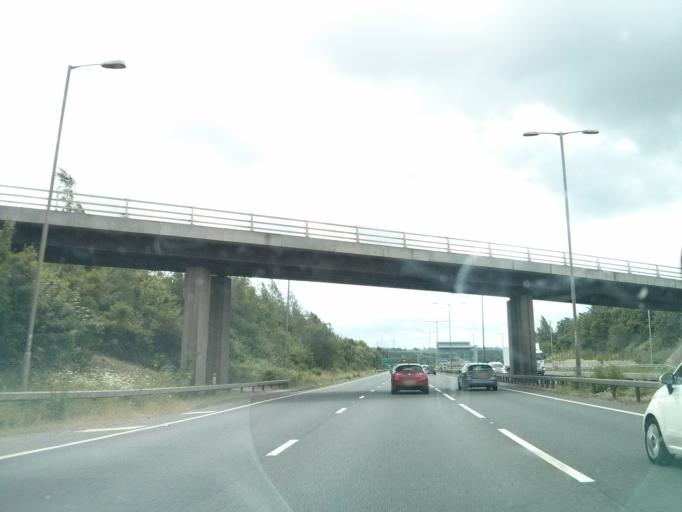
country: GB
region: England
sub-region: Northamptonshire
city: Kettering
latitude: 52.4035
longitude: -0.7515
